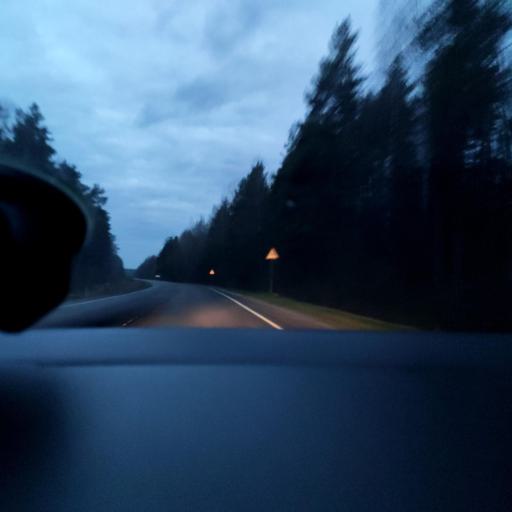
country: RU
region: Moskovskaya
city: Shaturtorf
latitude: 55.4275
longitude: 39.3232
